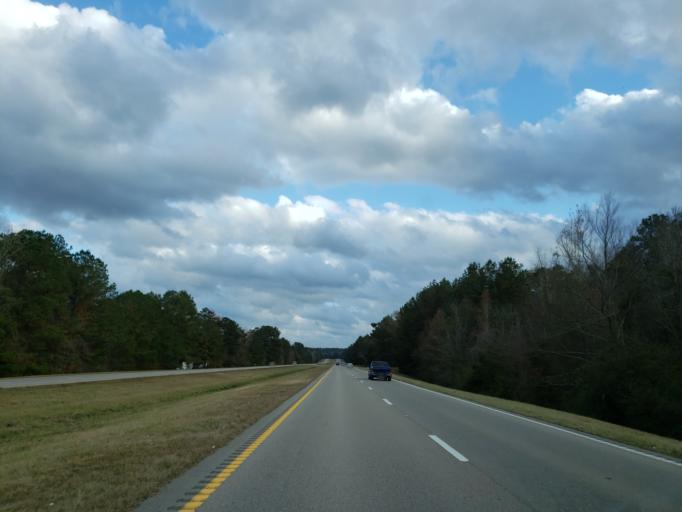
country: US
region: Mississippi
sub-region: Perry County
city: New Augusta
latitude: 31.2208
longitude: -89.1769
